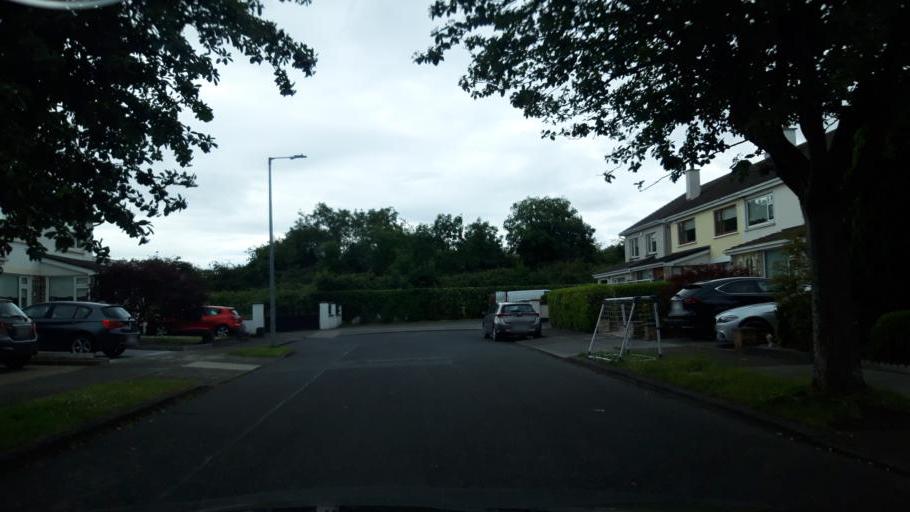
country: IE
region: Leinster
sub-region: Fingal County
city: Blanchardstown
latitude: 53.3796
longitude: -6.3870
